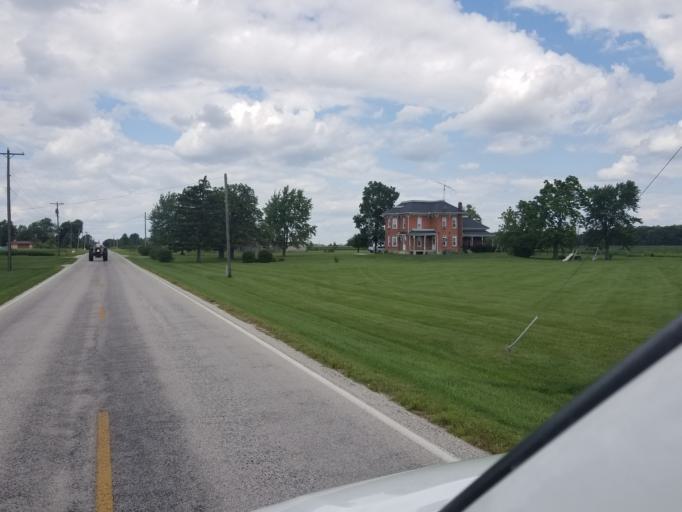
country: US
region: Ohio
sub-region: Ottawa County
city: Elmore
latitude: 41.5655
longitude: -83.2803
